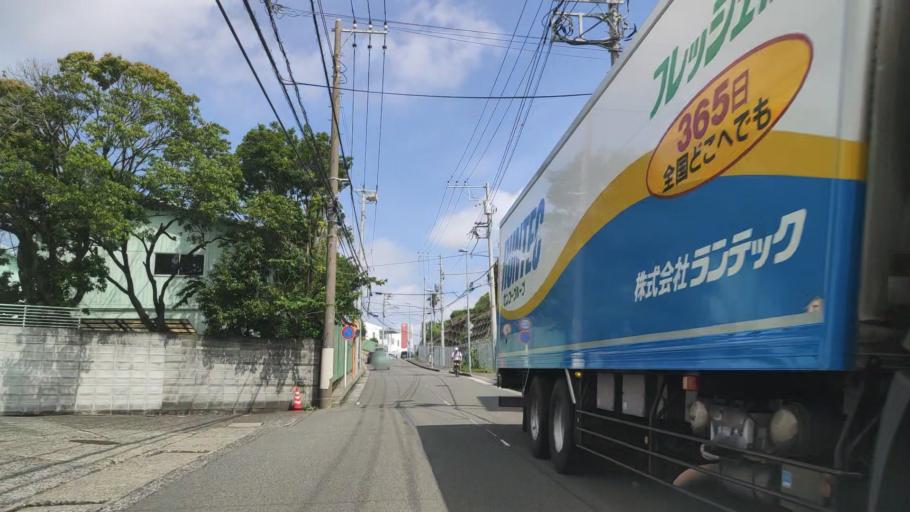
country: JP
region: Kanagawa
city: Minami-rinkan
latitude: 35.4244
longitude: 139.5366
